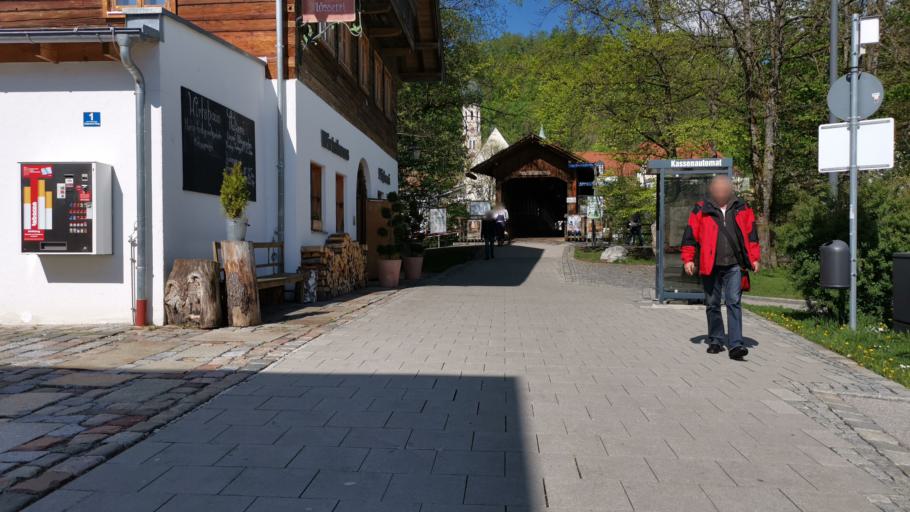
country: DE
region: Bavaria
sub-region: Upper Bavaria
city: Wolfratshausen
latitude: 47.9139
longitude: 11.4204
